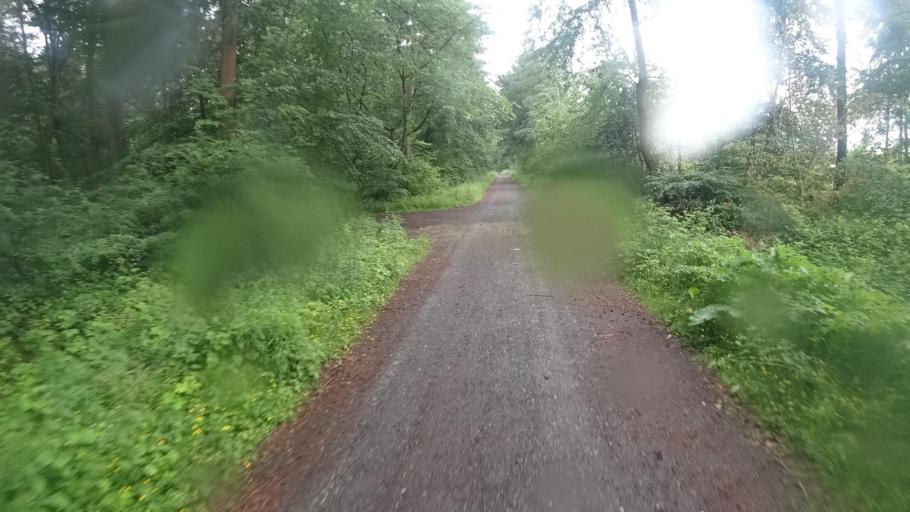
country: DE
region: Rheinland-Pfalz
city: Dernau
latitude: 50.5505
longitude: 7.0530
